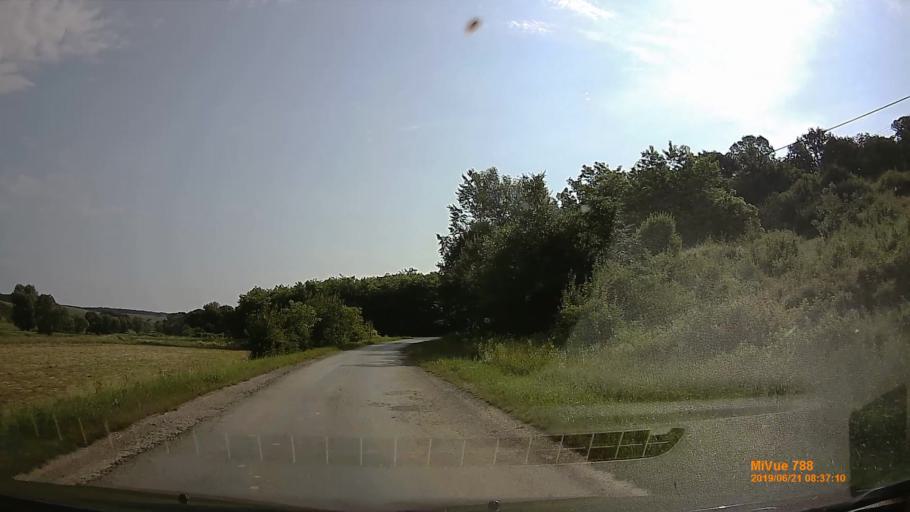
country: HU
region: Baranya
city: Buekkoesd
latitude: 46.1749
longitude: 17.9138
